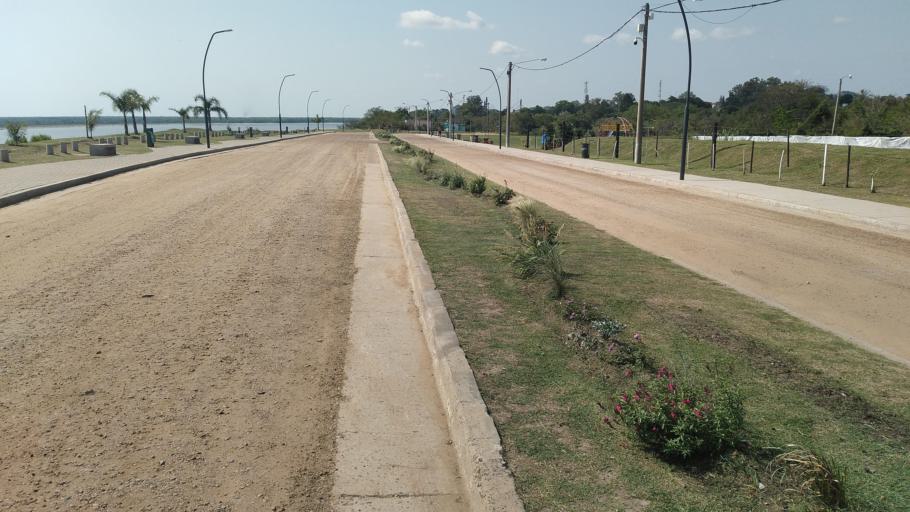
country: AR
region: Entre Rios
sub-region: Departamento de La Paz
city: La Paz
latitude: -30.7499
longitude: -59.6550
